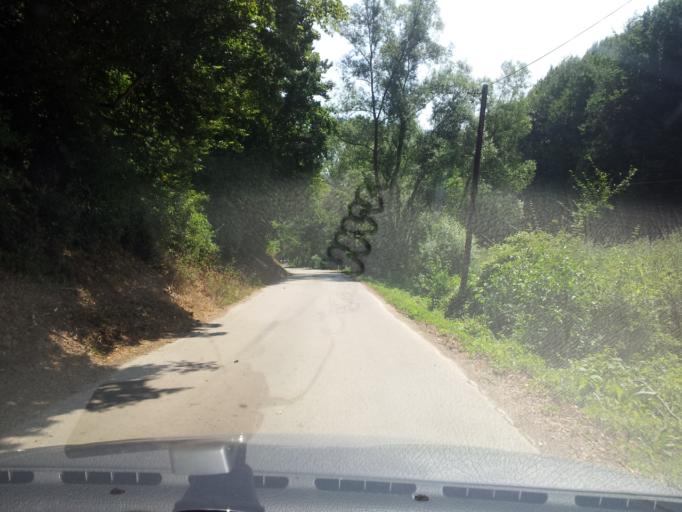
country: SK
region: Trenciansky
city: Nova Dubnica
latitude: 48.9061
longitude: 18.1146
